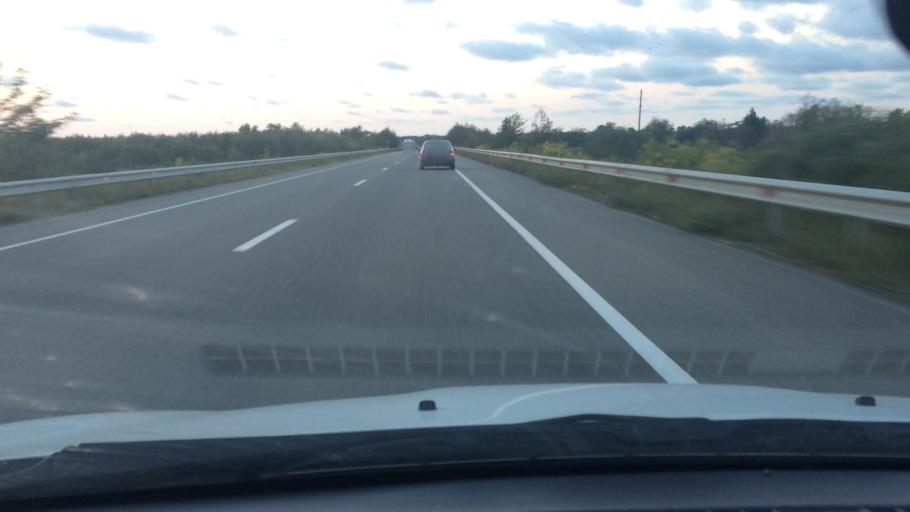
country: GE
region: Ajaria
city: Ochkhamuri
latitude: 41.9068
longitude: 41.7871
